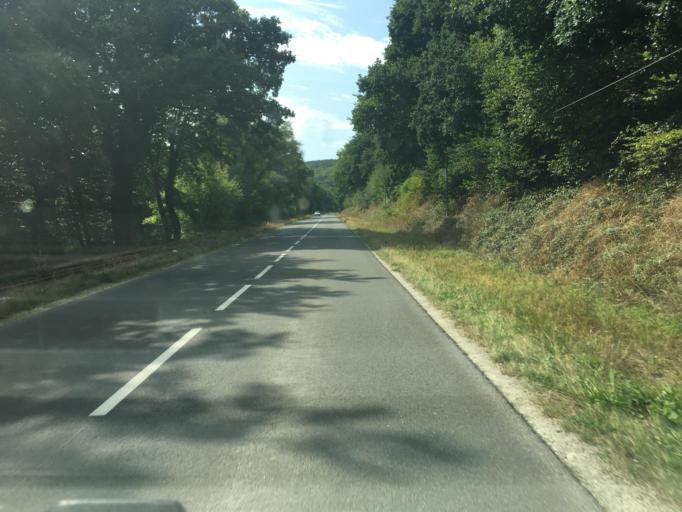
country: FR
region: Brittany
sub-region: Departement des Cotes-d'Armor
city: Gouarec
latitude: 48.2147
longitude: -3.1492
